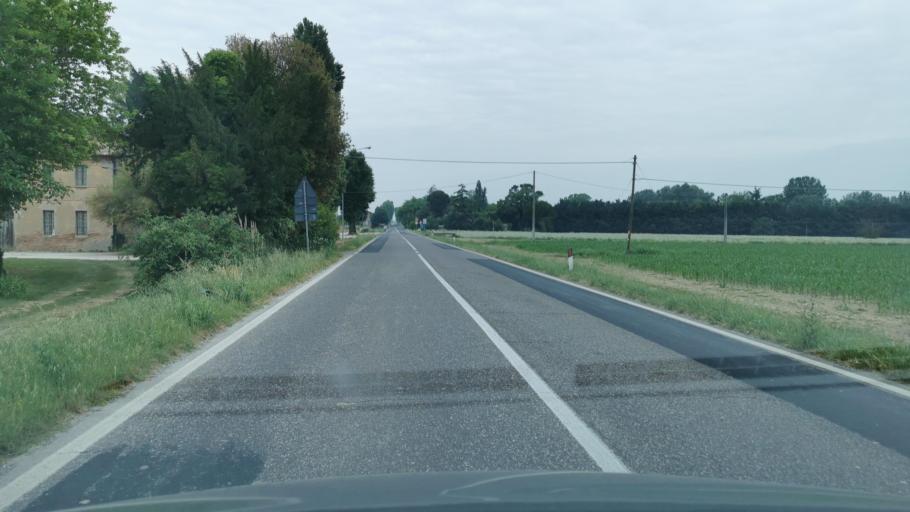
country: IT
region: Emilia-Romagna
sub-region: Provincia di Ravenna
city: Russi
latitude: 44.3967
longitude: 12.0354
